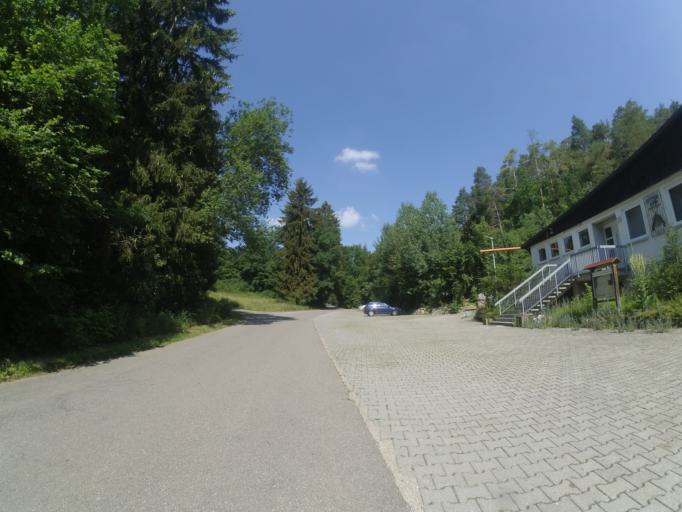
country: DE
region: Baden-Wuerttemberg
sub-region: Tuebingen Region
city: Dornstadt
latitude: 48.4551
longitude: 9.9024
